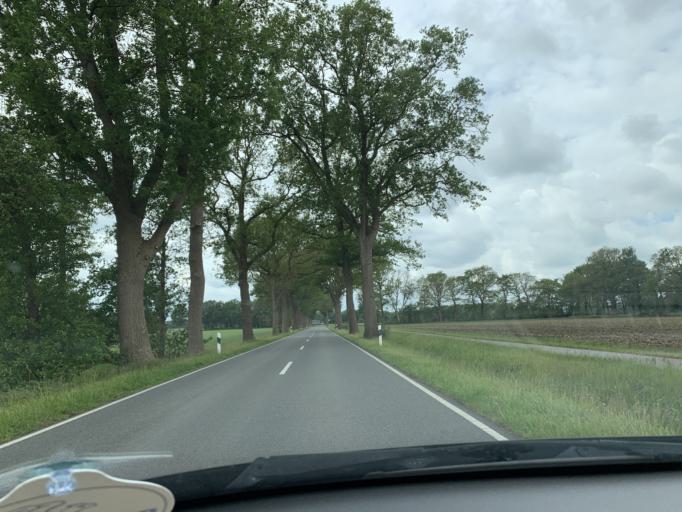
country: DE
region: Lower Saxony
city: Westerstede
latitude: 53.2953
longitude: 7.9927
